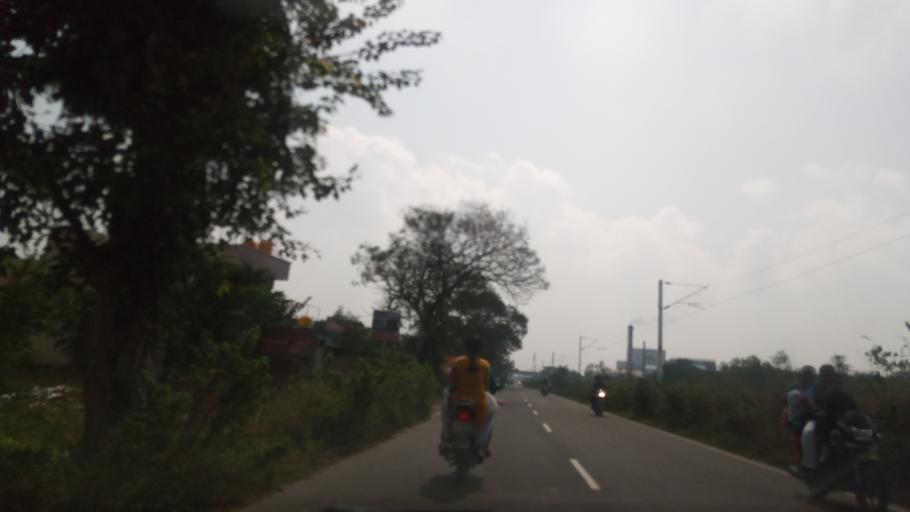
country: IN
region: Tamil Nadu
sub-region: Kancheepuram
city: Kanchipuram
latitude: 12.8805
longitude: 79.6891
